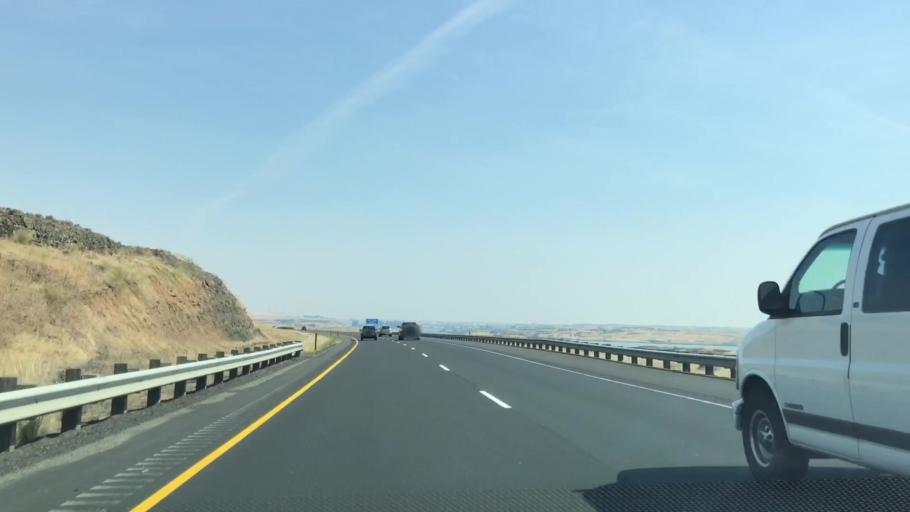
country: US
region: Washington
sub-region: Adams County
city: Ritzville
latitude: 47.2671
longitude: -118.0643
